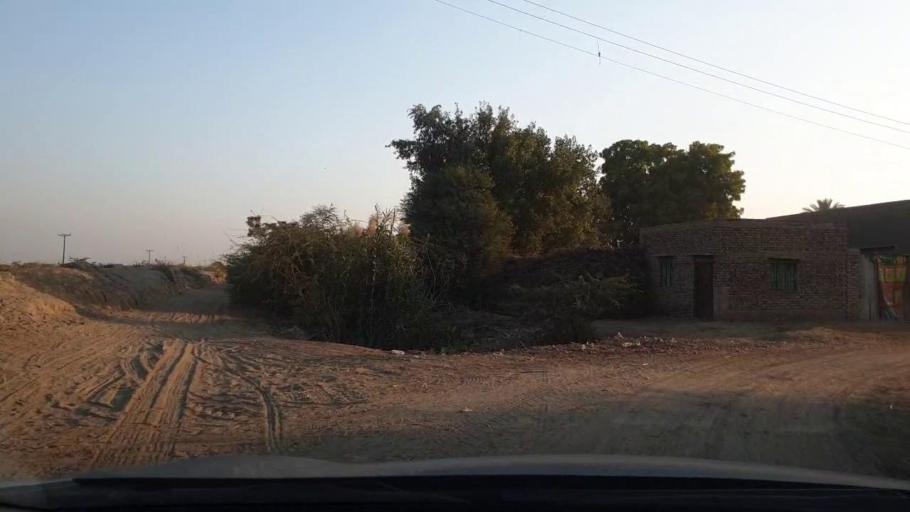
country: PK
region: Sindh
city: Tando Adam
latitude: 25.6830
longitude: 68.7458
